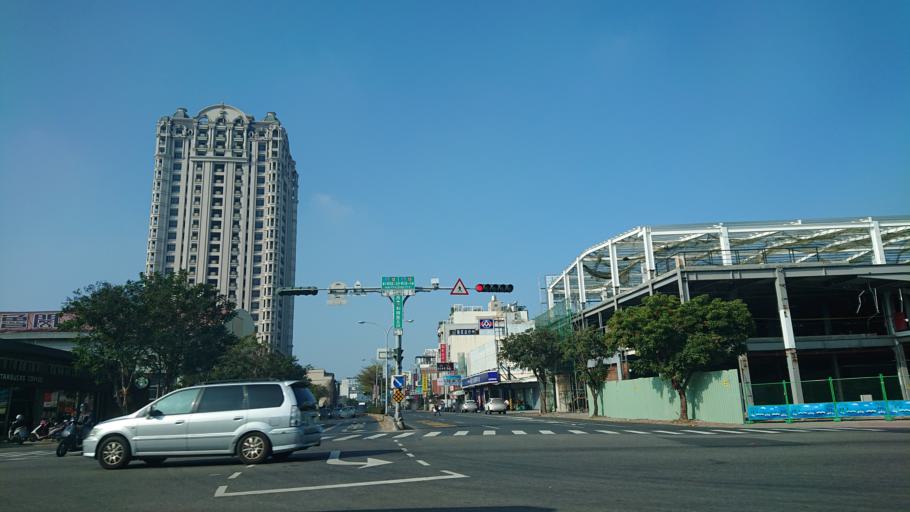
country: TW
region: Taiwan
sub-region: Tainan
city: Tainan
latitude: 23.0068
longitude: 120.1863
